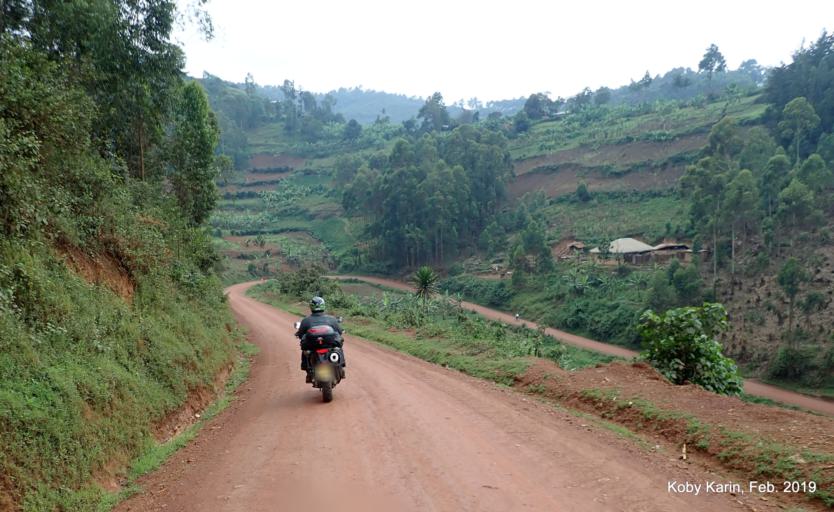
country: UG
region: Western Region
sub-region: Kabale District
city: Kabale
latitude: -1.2636
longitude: 29.9416
